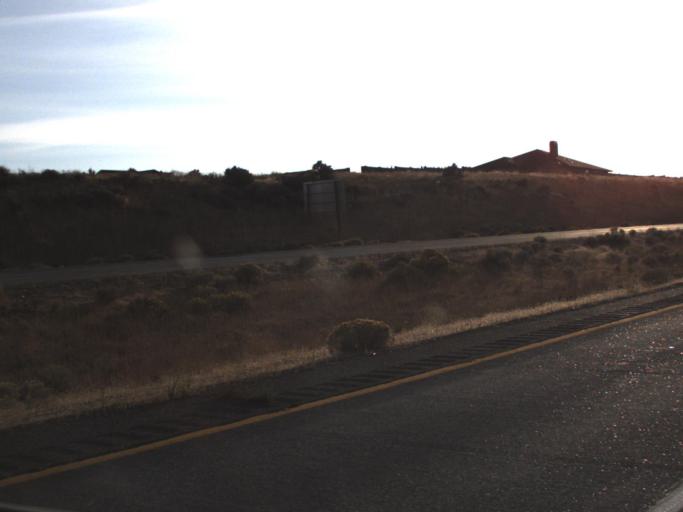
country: US
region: Washington
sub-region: Benton County
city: Richland
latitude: 46.1979
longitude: -119.3079
